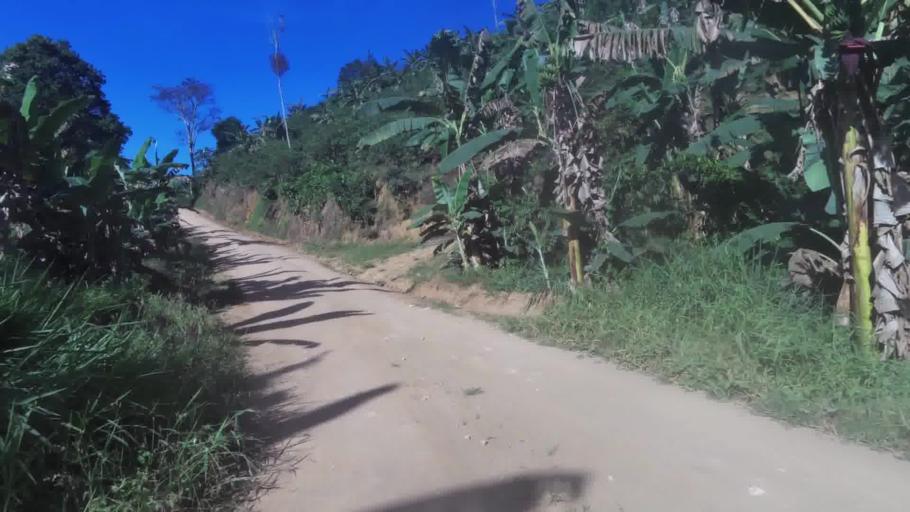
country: BR
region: Espirito Santo
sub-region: Iconha
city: Iconha
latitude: -20.7568
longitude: -40.8161
